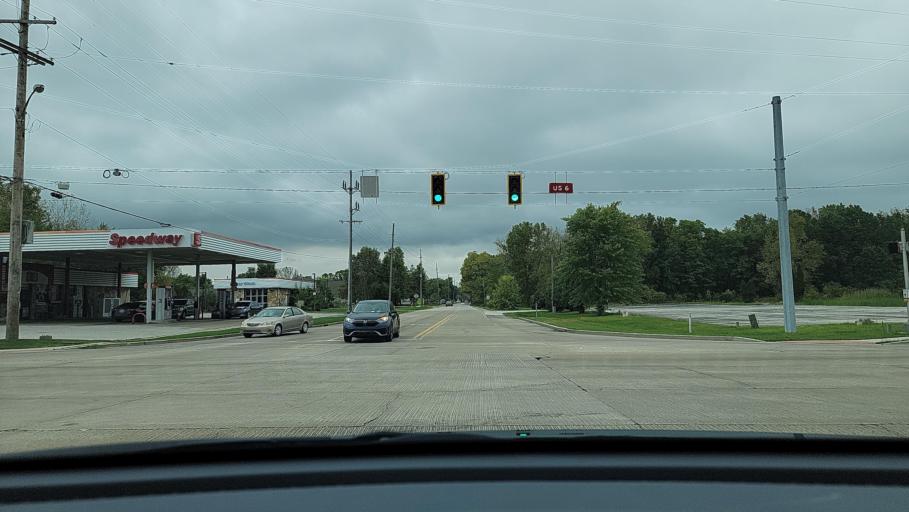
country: US
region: Indiana
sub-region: Porter County
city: Portage
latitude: 41.5505
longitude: -87.1971
